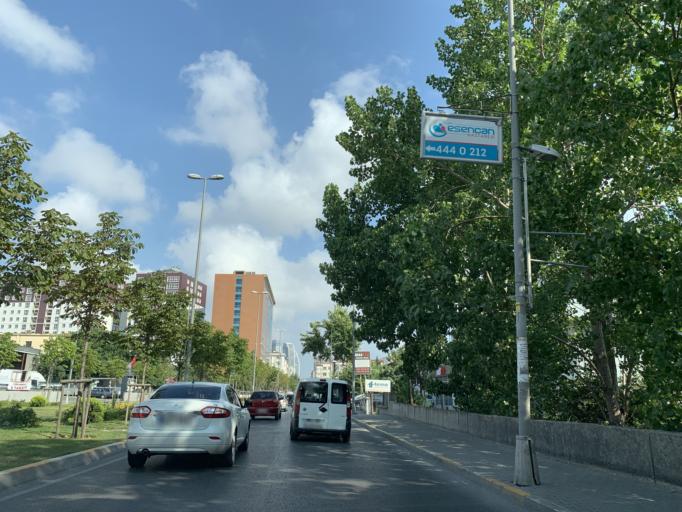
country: TR
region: Istanbul
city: Esenyurt
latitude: 41.0272
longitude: 28.6672
